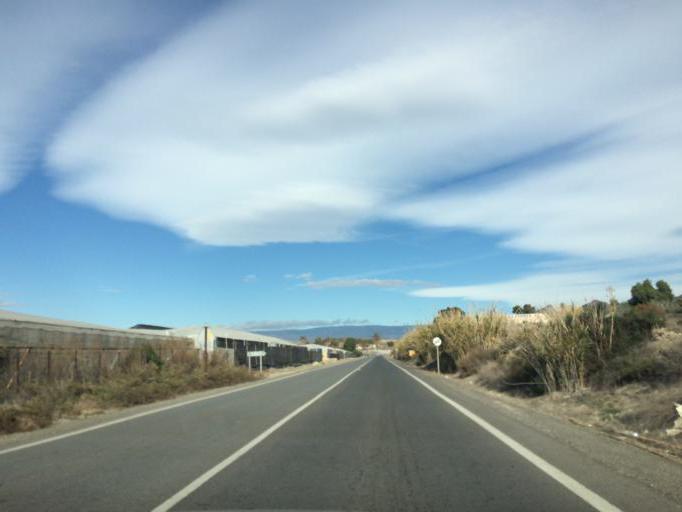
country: ES
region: Andalusia
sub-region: Provincia de Almeria
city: Pechina
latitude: 36.9227
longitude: -2.4460
